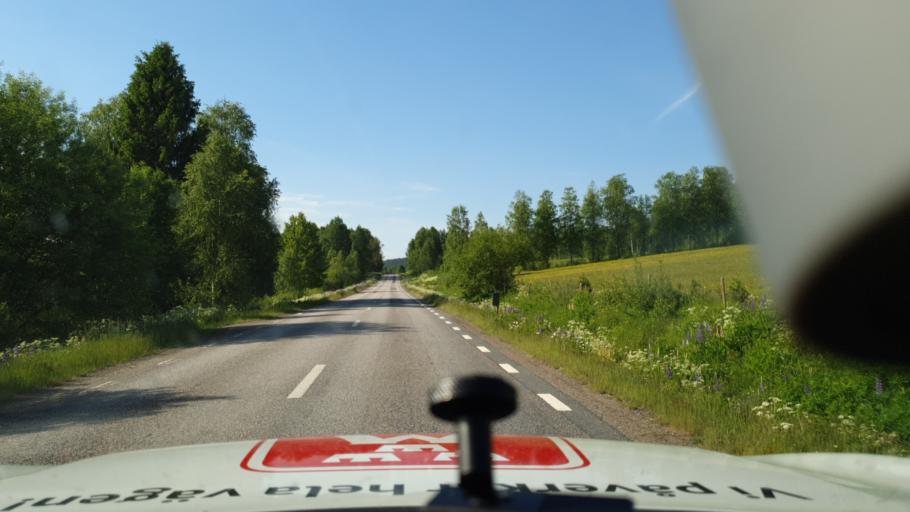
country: SE
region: Vaermland
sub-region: Torsby Kommun
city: Torsby
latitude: 59.9368
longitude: 12.9009
